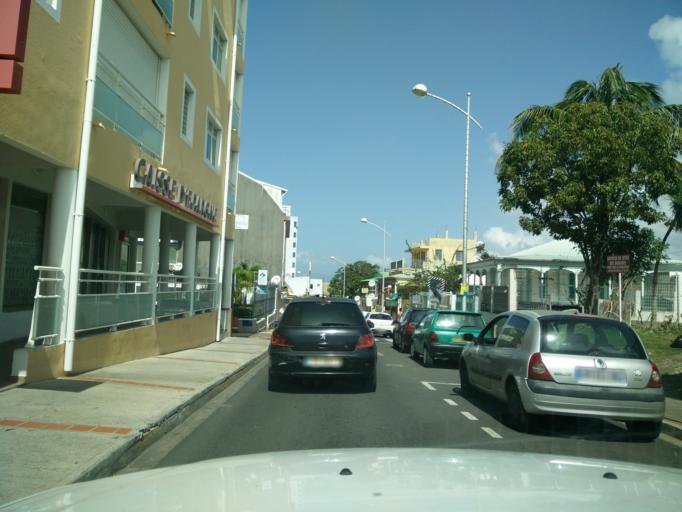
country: GP
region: Guadeloupe
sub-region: Guadeloupe
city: Le Gosier
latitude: 16.2063
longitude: -61.4929
